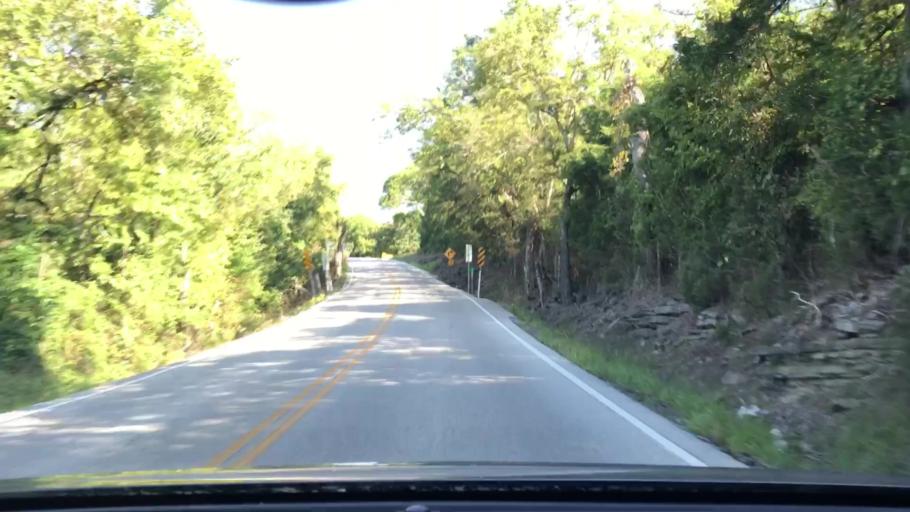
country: US
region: Tennessee
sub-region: Smith County
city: Carthage
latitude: 36.2713
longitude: -85.9575
